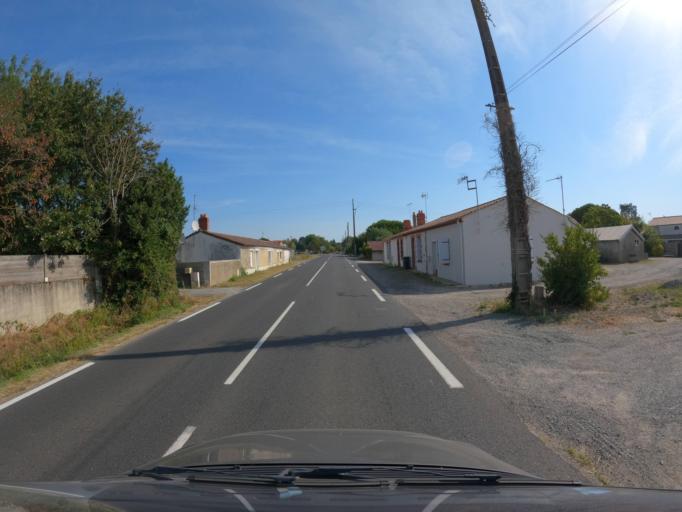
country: FR
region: Pays de la Loire
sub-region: Departement de la Vendee
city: Saint-Christophe-du-Ligneron
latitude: 46.8173
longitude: -1.7674
